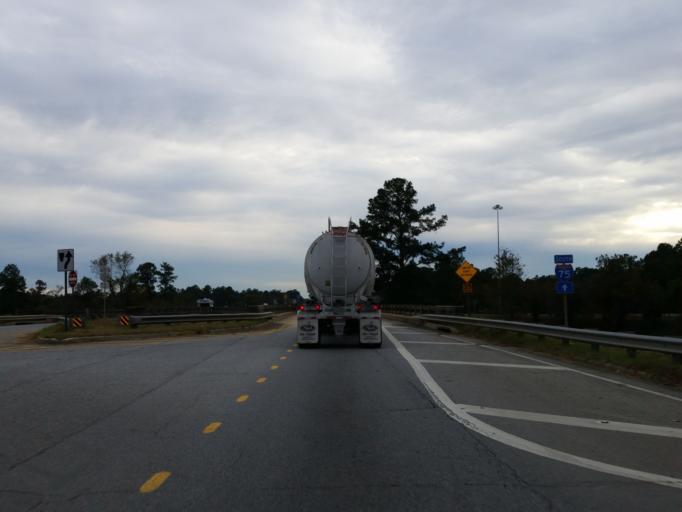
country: US
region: Georgia
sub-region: Lowndes County
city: Valdosta
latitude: 30.7519
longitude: -83.2734
